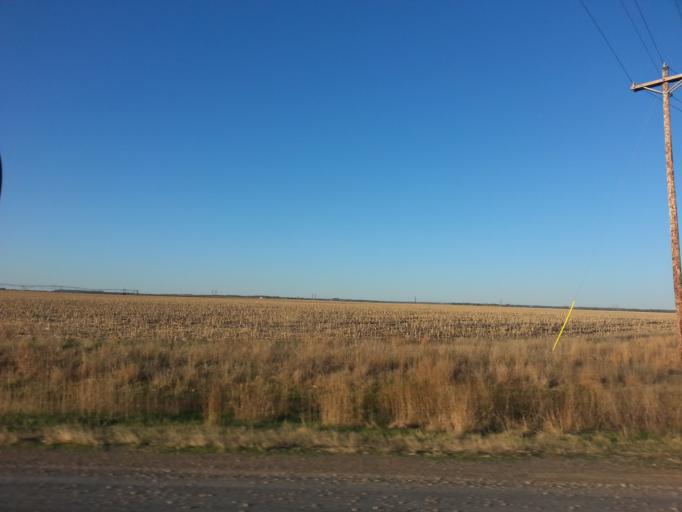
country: US
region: Wisconsin
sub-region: Pierce County
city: Prescott
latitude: 44.6876
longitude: -92.8095
